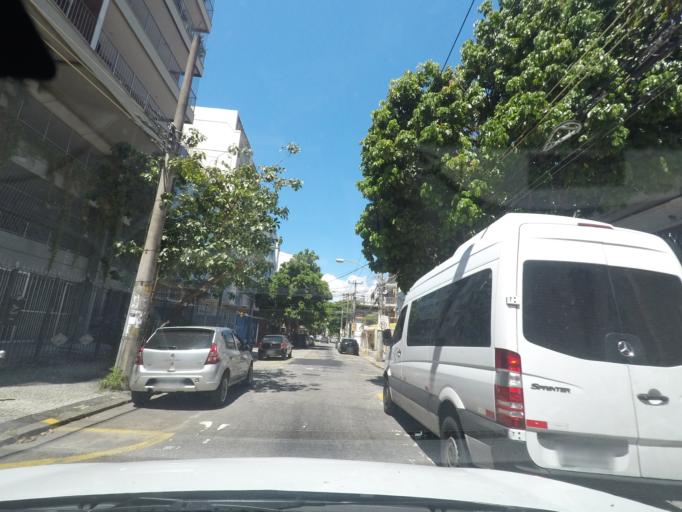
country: BR
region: Rio de Janeiro
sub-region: Rio De Janeiro
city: Rio de Janeiro
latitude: -22.9185
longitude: -43.2387
